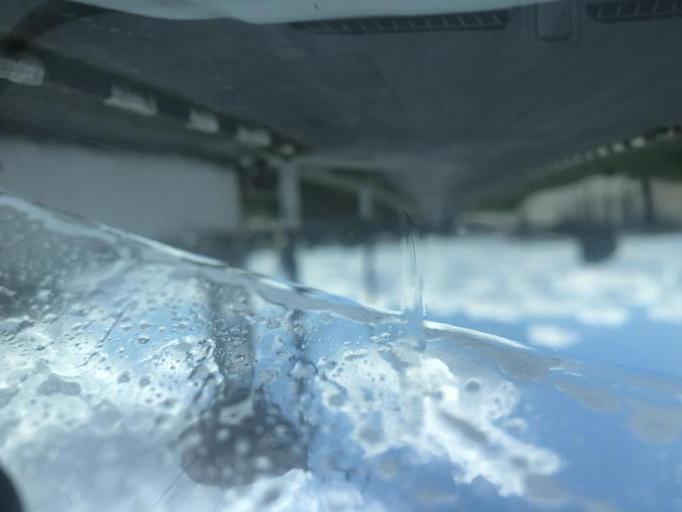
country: BR
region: Santa Catarina
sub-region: Lages
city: Lages
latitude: -27.7910
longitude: -50.3118
